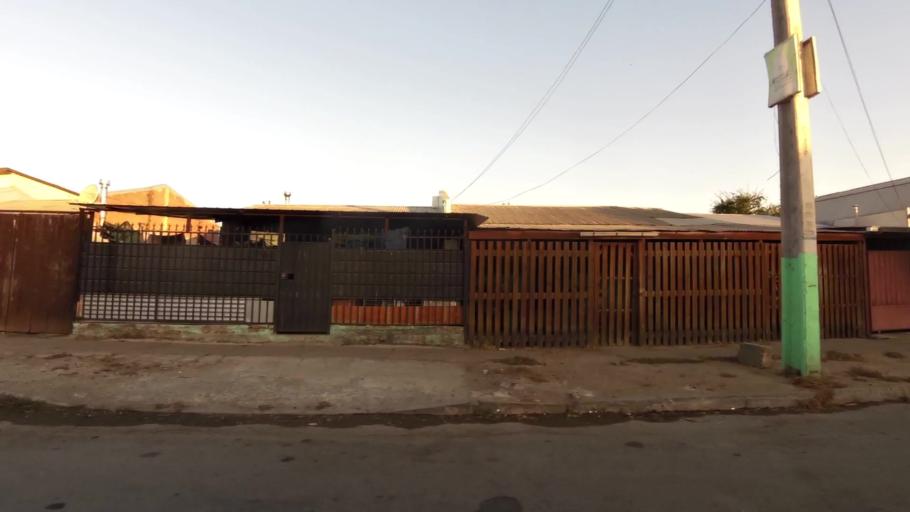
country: CL
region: Maule
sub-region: Provincia de Talca
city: Talca
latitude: -35.4456
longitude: -71.6400
